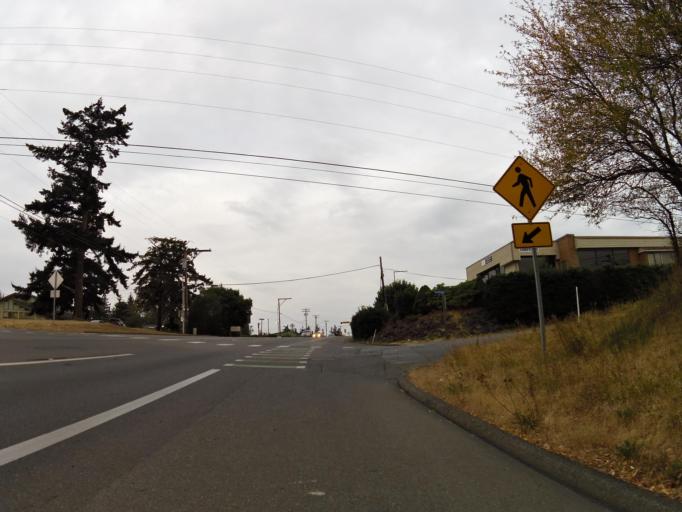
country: US
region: Washington
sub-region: Jefferson County
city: Port Townsend
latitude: 48.1029
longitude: -122.7900
